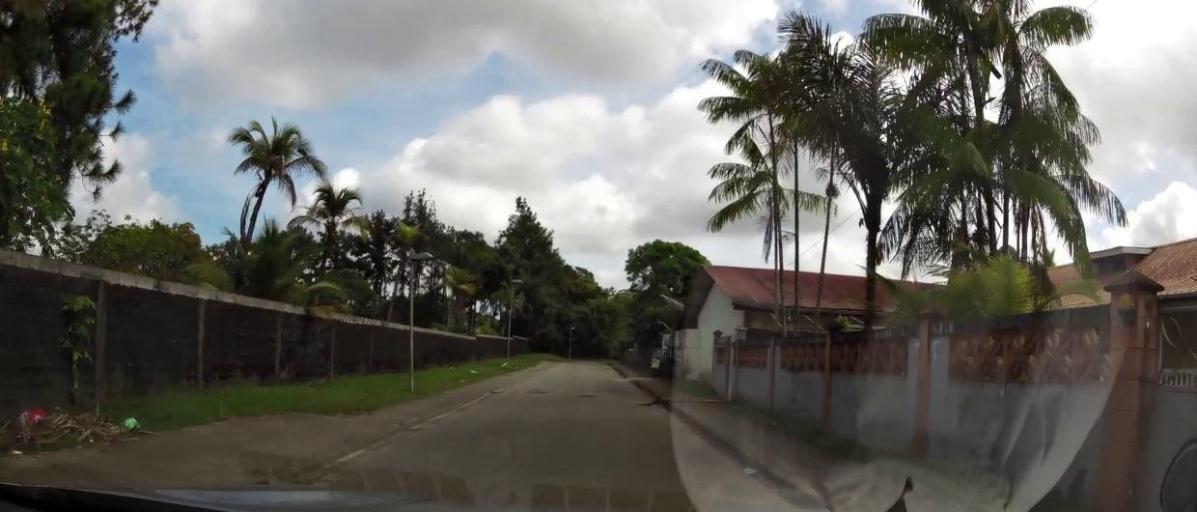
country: GF
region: Guyane
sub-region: Guyane
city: Matoury
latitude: 4.8737
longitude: -52.3268
